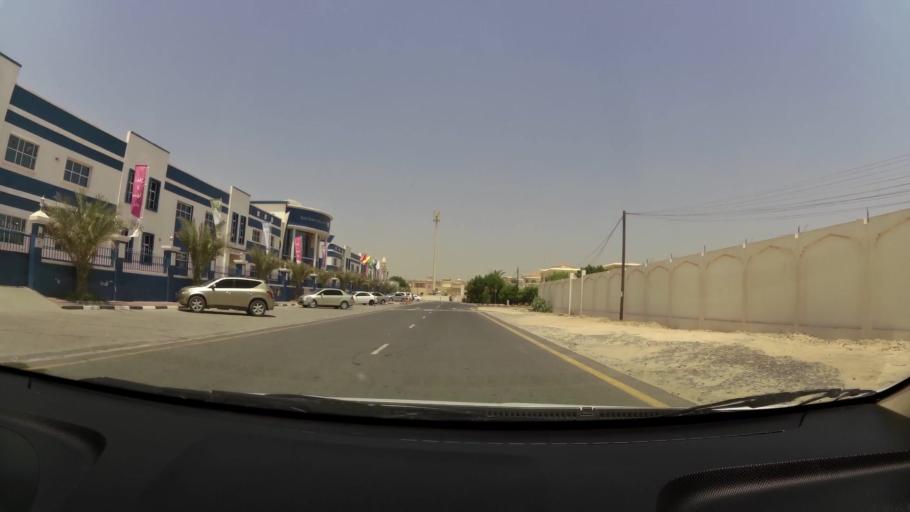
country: AE
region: Ajman
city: Ajman
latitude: 25.4031
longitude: 55.5210
